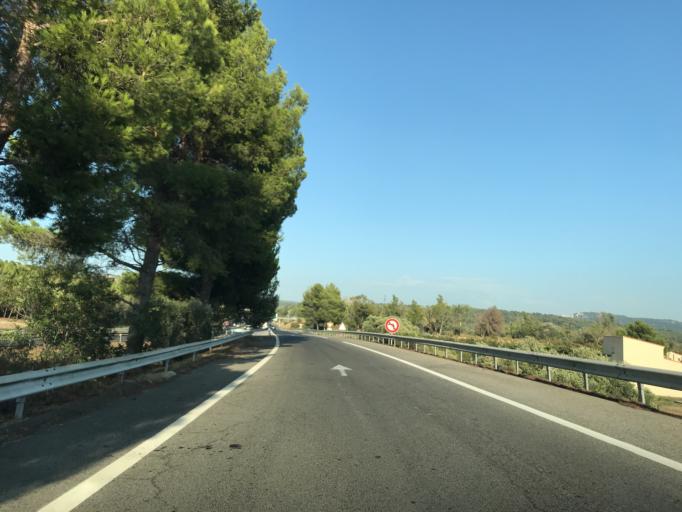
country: FR
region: Provence-Alpes-Cote d'Azur
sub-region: Departement des Bouches-du-Rhone
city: Coudoux
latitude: 43.5510
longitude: 5.2392
